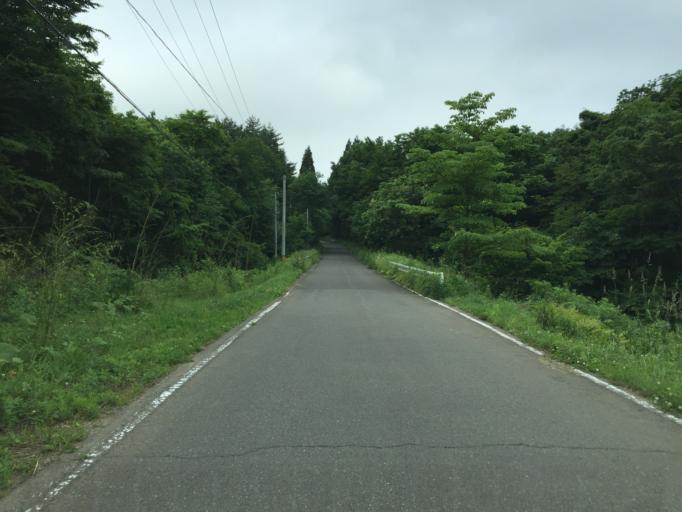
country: JP
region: Fukushima
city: Yanagawamachi-saiwaicho
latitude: 37.7901
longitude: 140.7111
